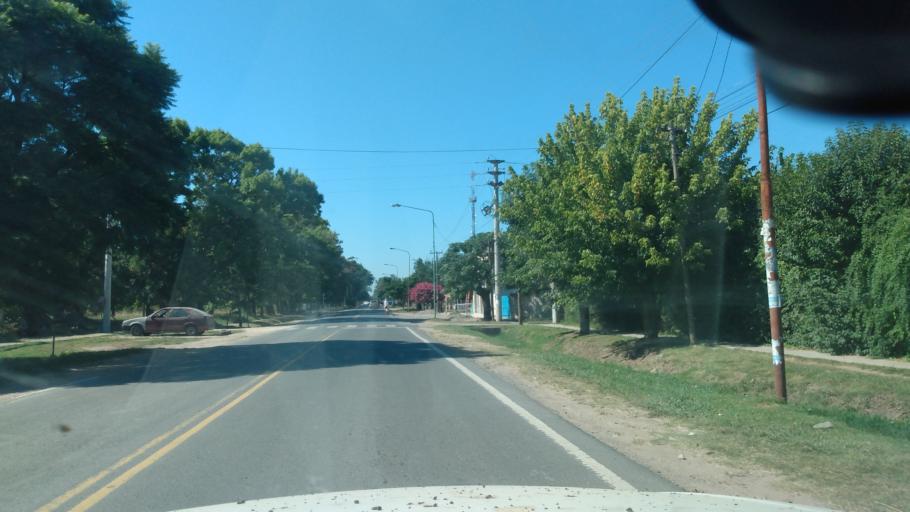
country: AR
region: Buenos Aires
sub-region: Partido de Lujan
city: Lujan
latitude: -34.4956
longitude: -59.0743
